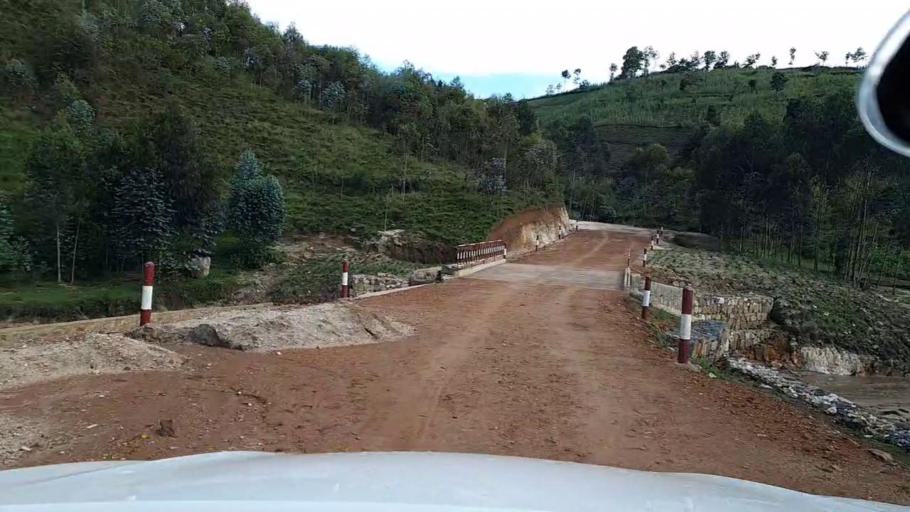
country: BI
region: Kayanza
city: Kayanza
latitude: -2.7798
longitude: 29.4508
